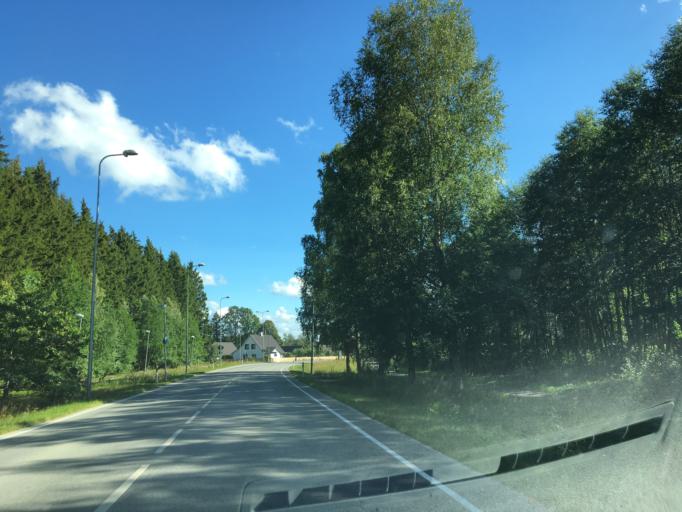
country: EE
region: Paernumaa
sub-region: Vaendra vald (alev)
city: Vandra
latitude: 58.6249
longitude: 25.1055
